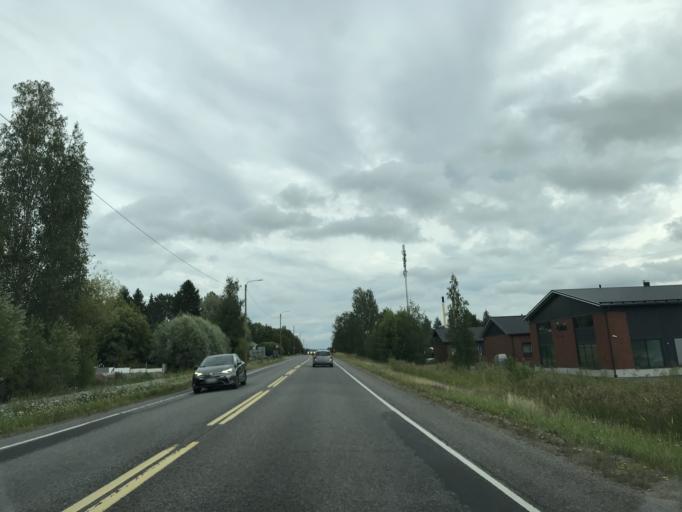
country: FI
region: Varsinais-Suomi
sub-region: Turku
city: Kaarina
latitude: 60.4108
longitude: 22.4070
